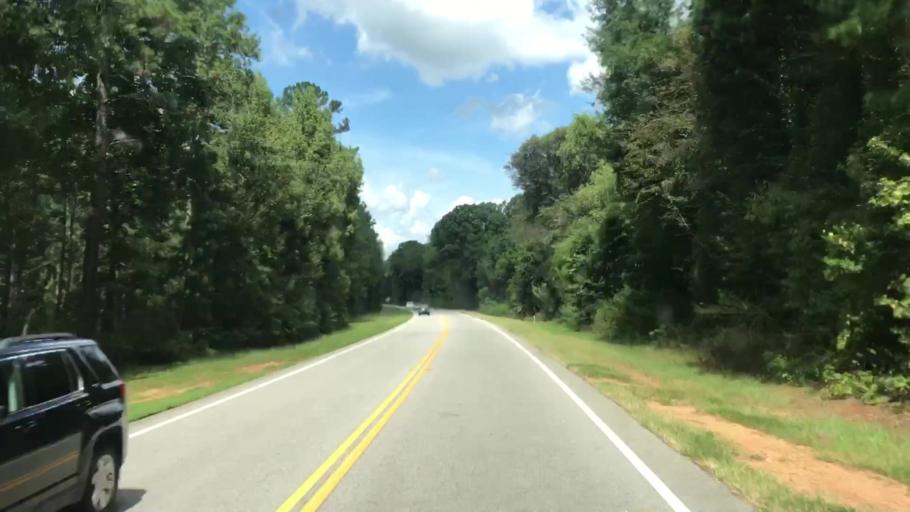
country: US
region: Georgia
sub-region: Greene County
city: Greensboro
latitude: 33.6951
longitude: -83.2776
